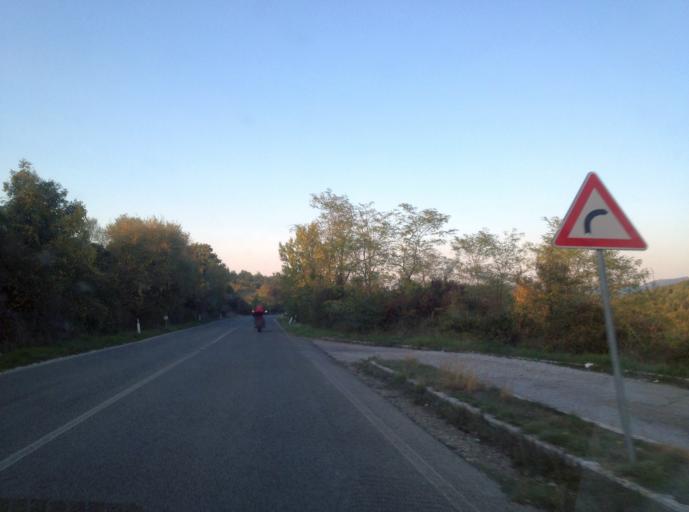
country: IT
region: Tuscany
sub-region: Provincia di Siena
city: Castellina in Chianti
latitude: 43.4805
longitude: 11.2979
